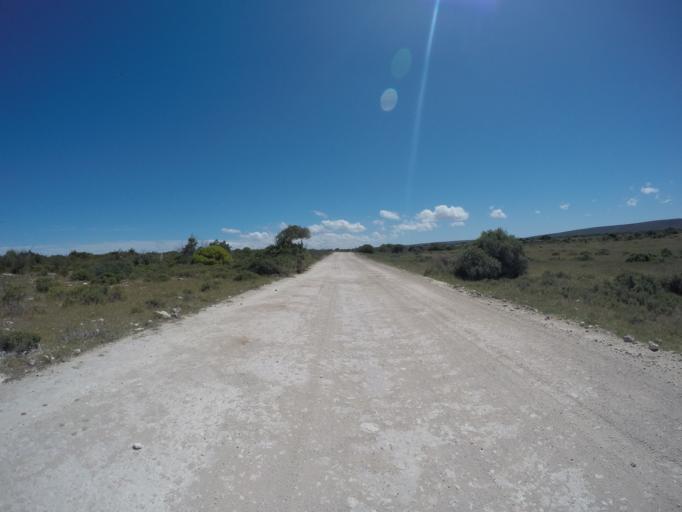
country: ZA
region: Western Cape
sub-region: Overberg District Municipality
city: Bredasdorp
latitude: -34.4564
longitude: 20.4154
